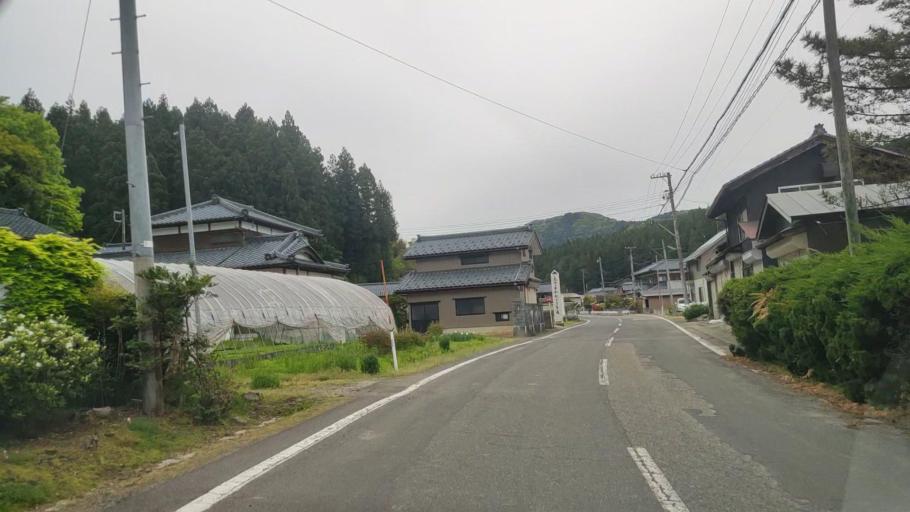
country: JP
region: Niigata
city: Gosen
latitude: 37.7247
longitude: 139.1351
